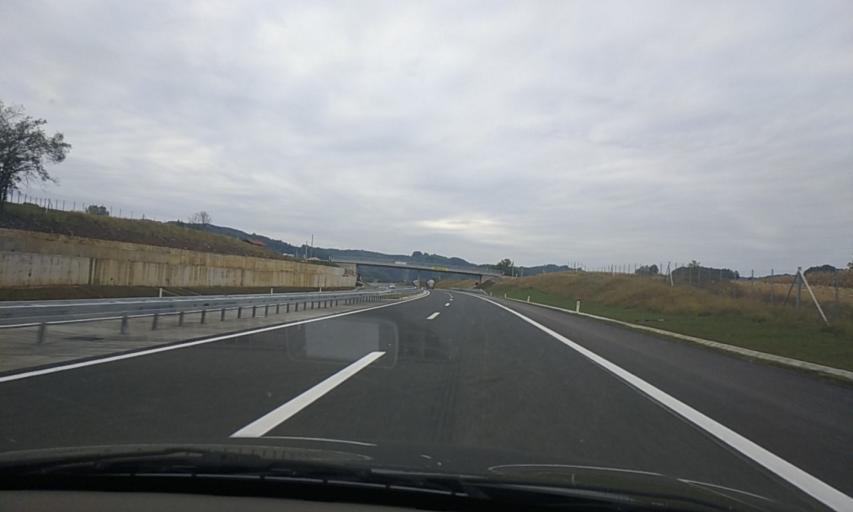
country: BA
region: Republika Srpska
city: Maglajani
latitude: 44.8597
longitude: 17.4664
